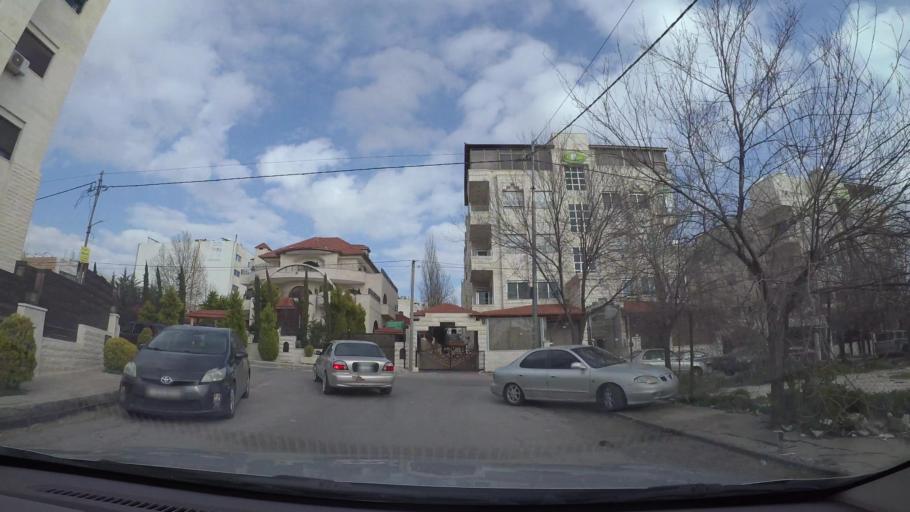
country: JO
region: Amman
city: Wadi as Sir
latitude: 31.9789
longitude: 35.8445
